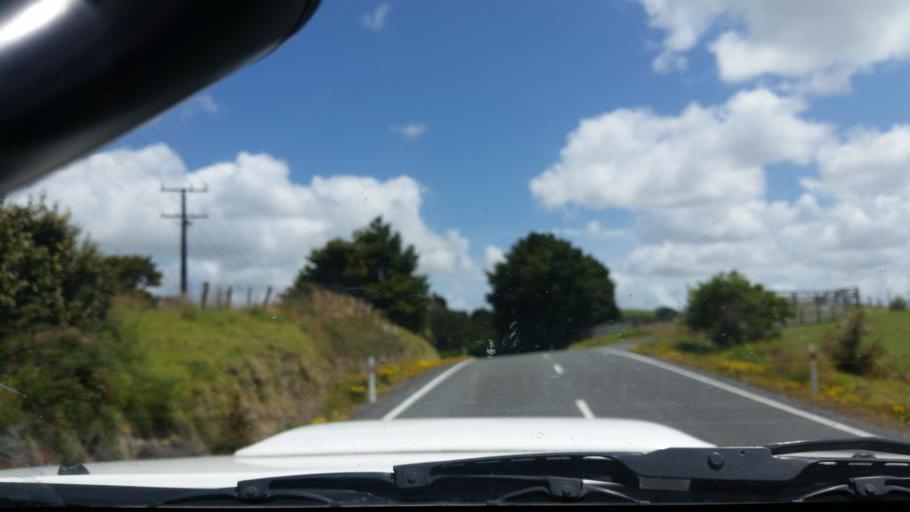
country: NZ
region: Northland
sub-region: Whangarei
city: Ruakaka
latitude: -36.0603
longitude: 174.2724
